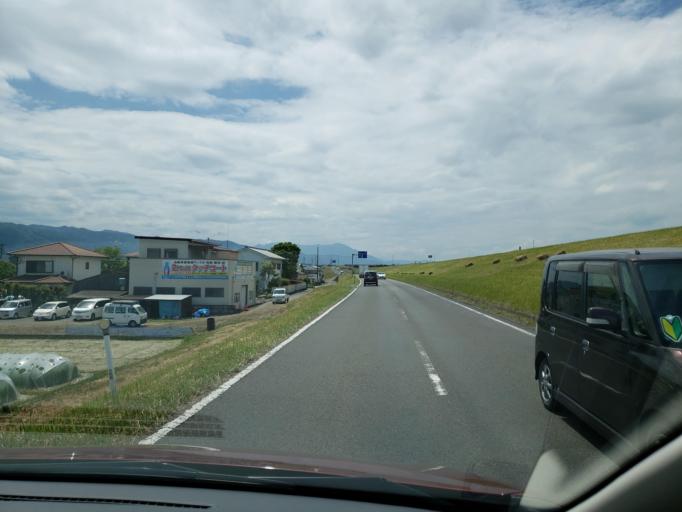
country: JP
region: Tokushima
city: Kamojimacho-jogejima
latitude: 34.0886
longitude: 134.3933
